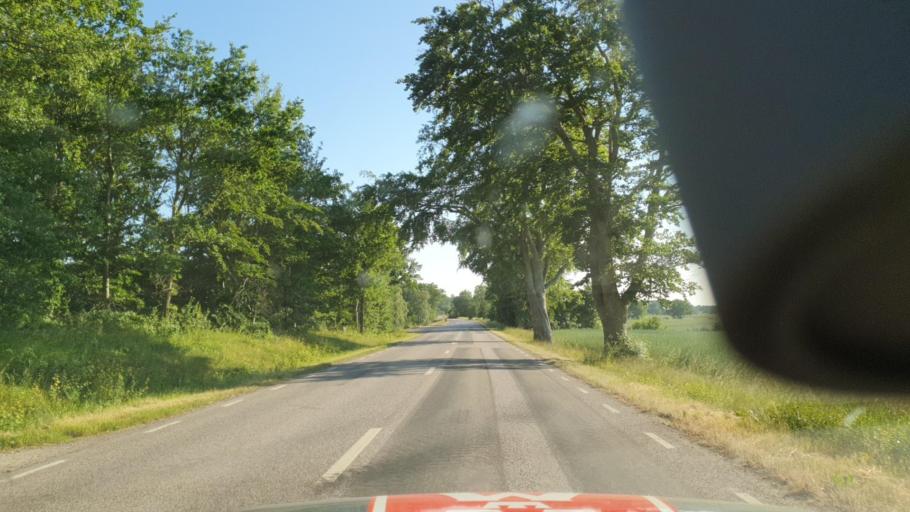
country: SE
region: Kalmar
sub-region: Kalmar Kommun
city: Ljungbyholm
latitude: 56.5253
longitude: 16.1697
